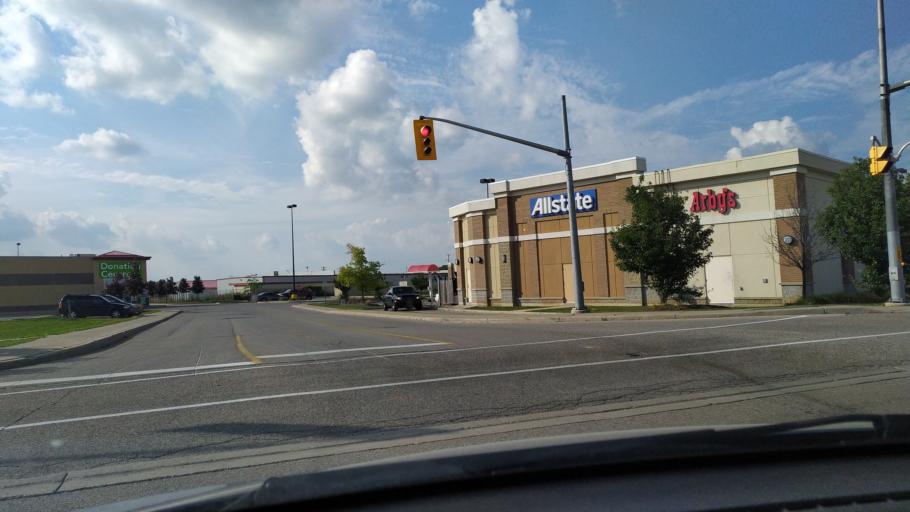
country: CA
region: Ontario
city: Waterloo
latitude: 43.5104
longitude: -80.5494
